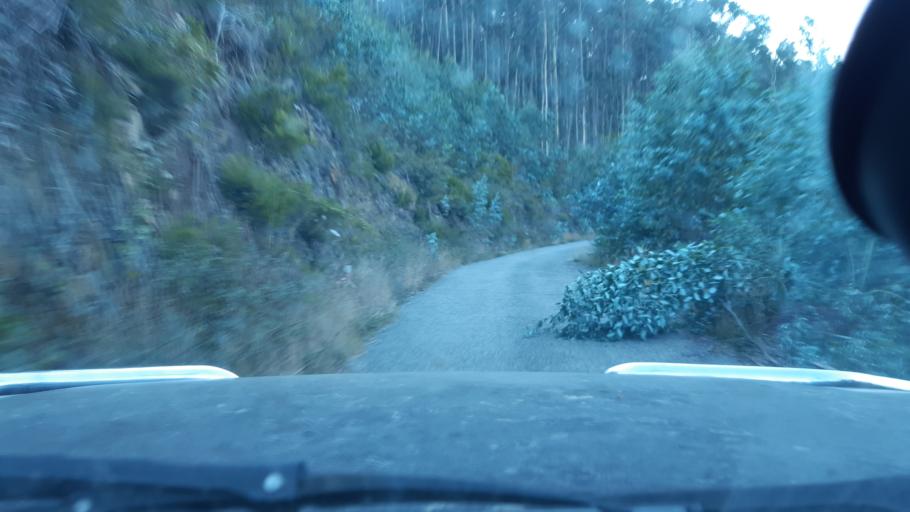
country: PT
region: Viseu
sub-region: Mortagua
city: Mortagua
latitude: 40.5213
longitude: -8.2520
